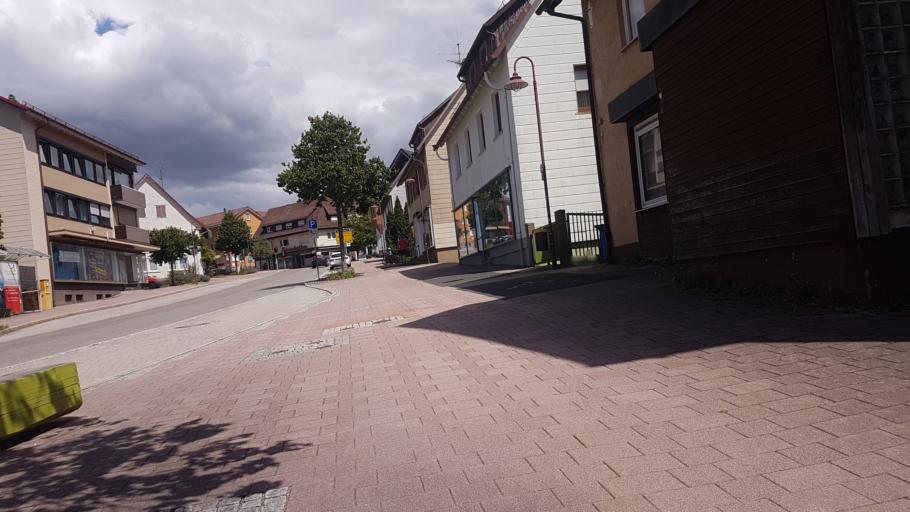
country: DE
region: Baden-Wuerttemberg
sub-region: Freiburg Region
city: Schramberg
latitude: 48.2278
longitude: 8.4185
